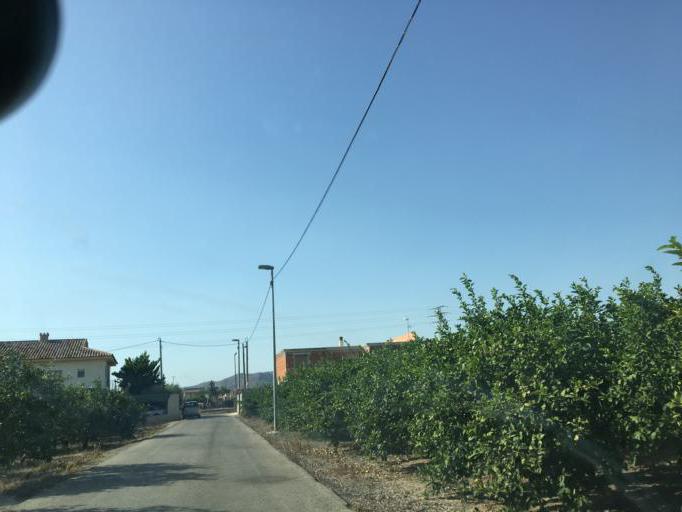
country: ES
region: Murcia
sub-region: Murcia
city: Santomera
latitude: 38.0316
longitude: -1.0580
